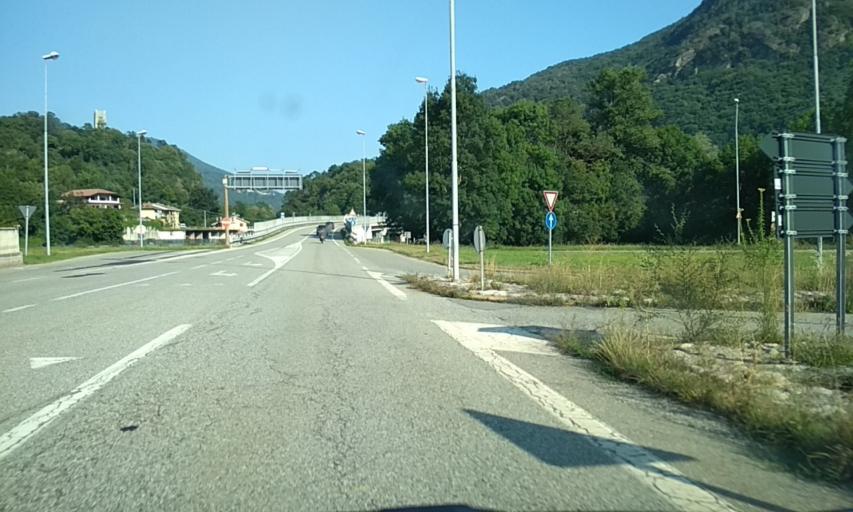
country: IT
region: Piedmont
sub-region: Provincia di Torino
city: Alpette
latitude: 45.4204
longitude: 7.5835
